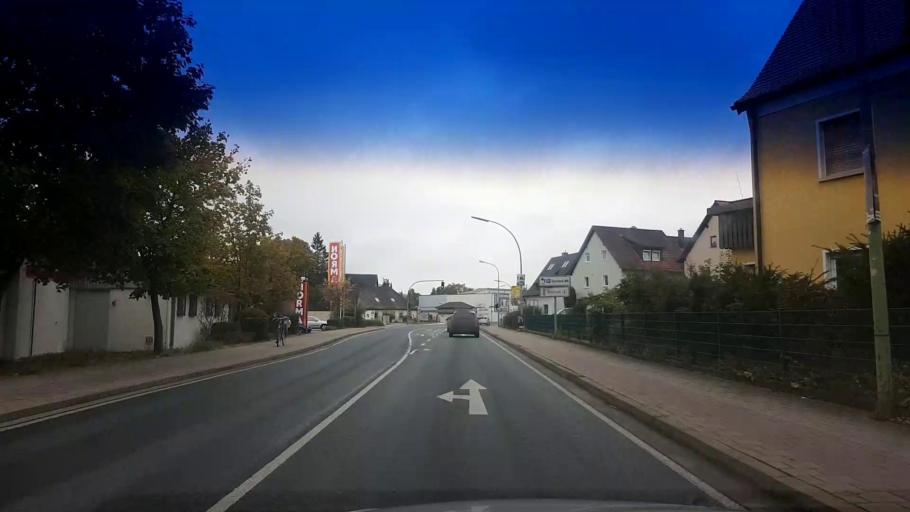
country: DE
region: Bavaria
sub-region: Upper Franconia
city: Forchheim
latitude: 49.7239
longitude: 11.0486
